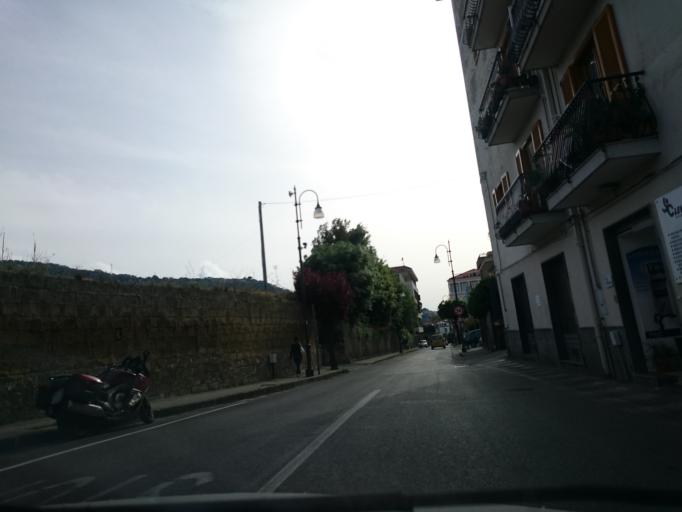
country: IT
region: Campania
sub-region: Provincia di Napoli
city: Sant'Agnello
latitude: 40.6316
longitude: 14.4052
